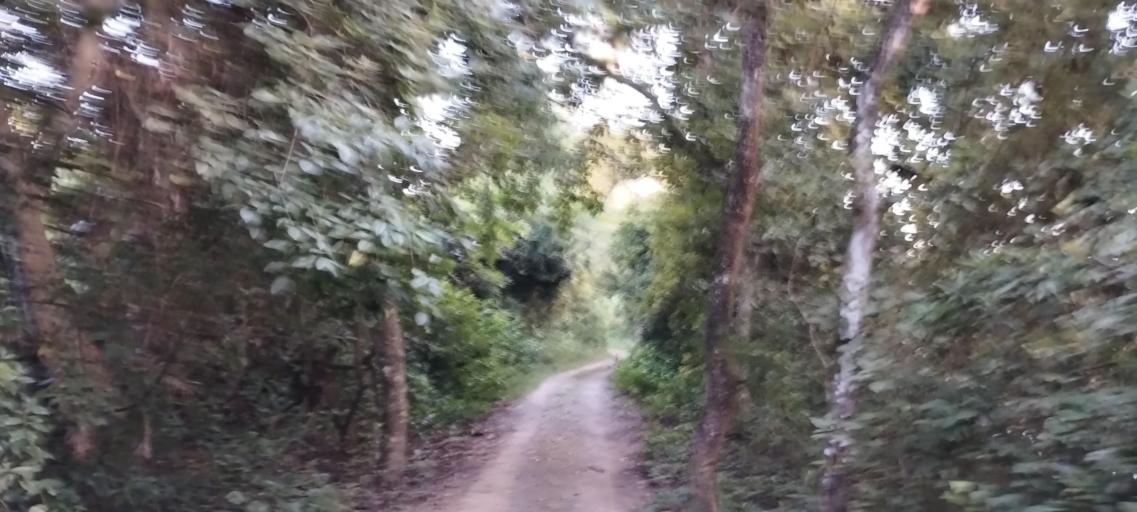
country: NP
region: Far Western
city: Tikapur
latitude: 28.4593
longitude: 81.2418
